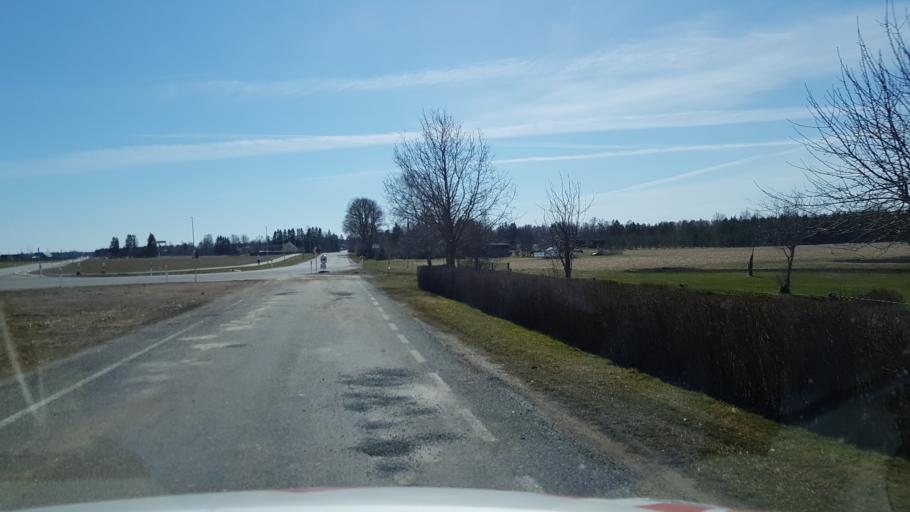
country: EE
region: Laeaene-Virumaa
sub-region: Vinni vald
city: Vinni
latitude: 59.2751
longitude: 26.4325
